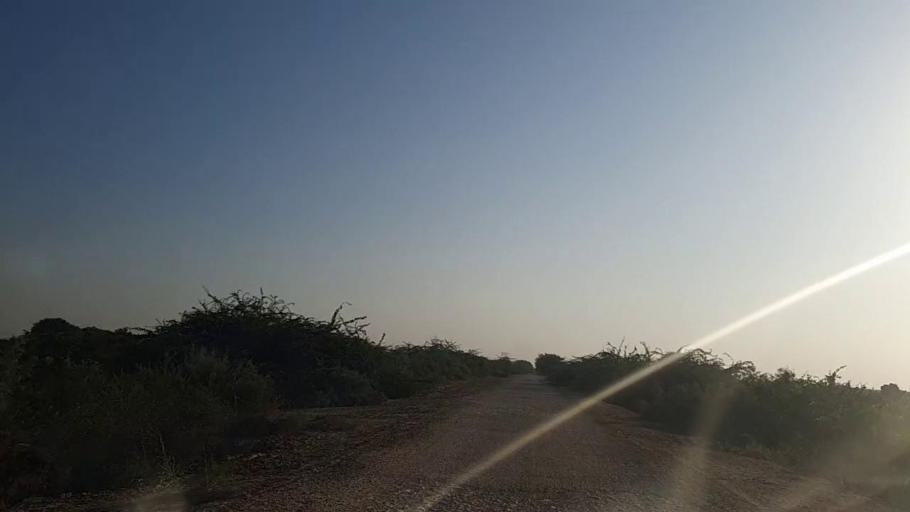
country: PK
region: Sindh
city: Jati
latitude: 24.4294
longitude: 68.1902
